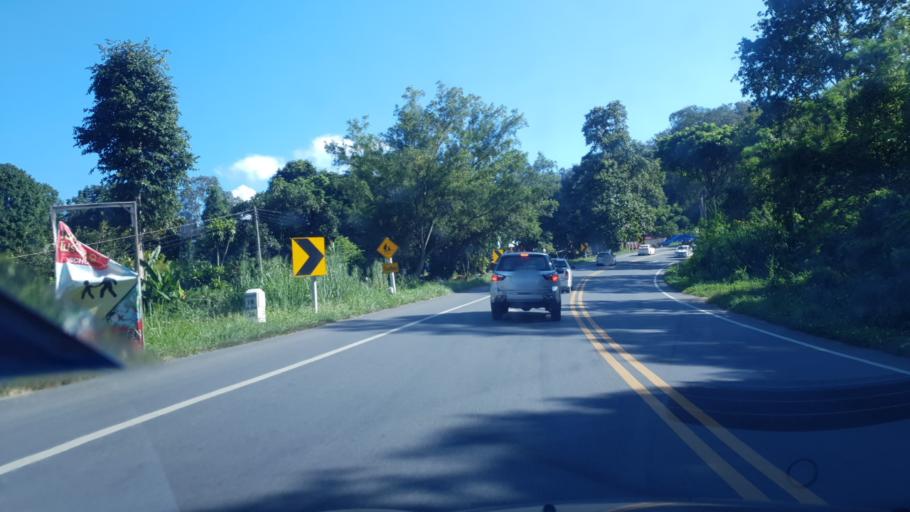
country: TH
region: Chiang Mai
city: Mae On
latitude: 18.9566
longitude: 99.2350
